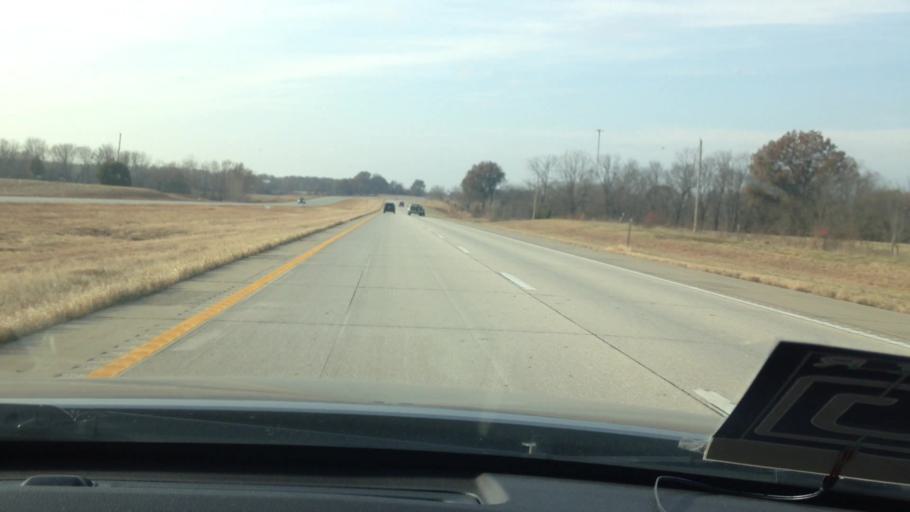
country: US
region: Missouri
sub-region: Henry County
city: Clinton
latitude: 38.4387
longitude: -93.9441
